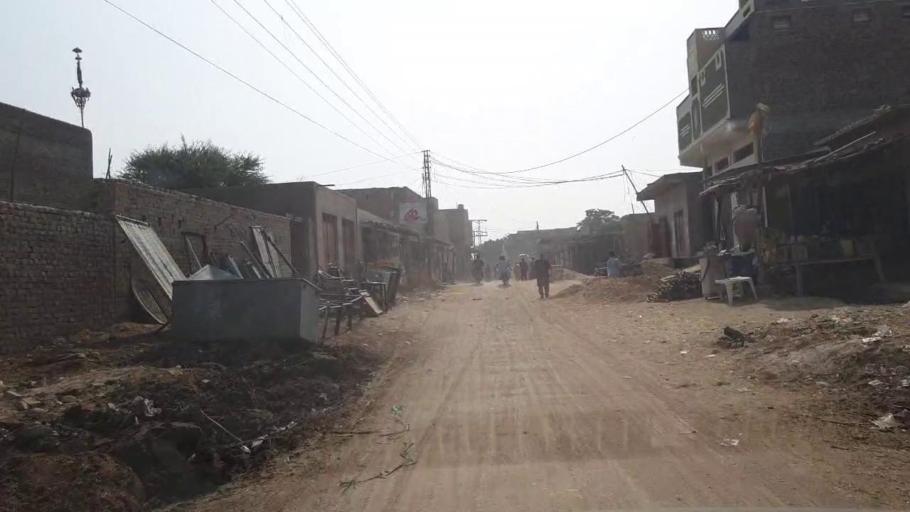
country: PK
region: Sindh
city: Bhit Shah
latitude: 25.8098
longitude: 68.4883
